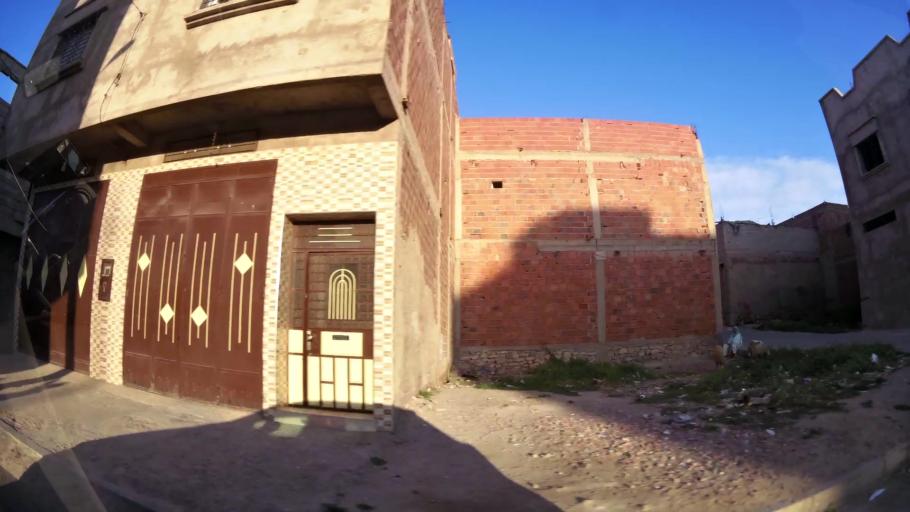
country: MA
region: Oriental
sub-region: Oujda-Angad
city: Oujda
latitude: 34.7100
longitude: -1.9074
